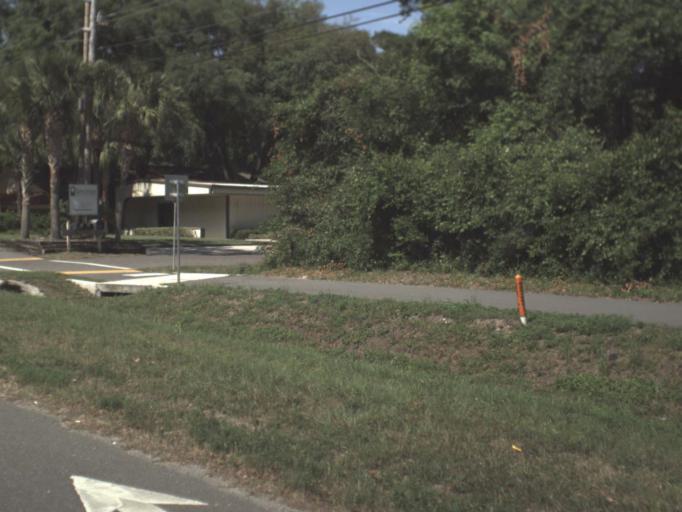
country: US
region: Florida
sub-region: Nassau County
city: Fernandina Beach
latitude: 30.5783
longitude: -81.4539
